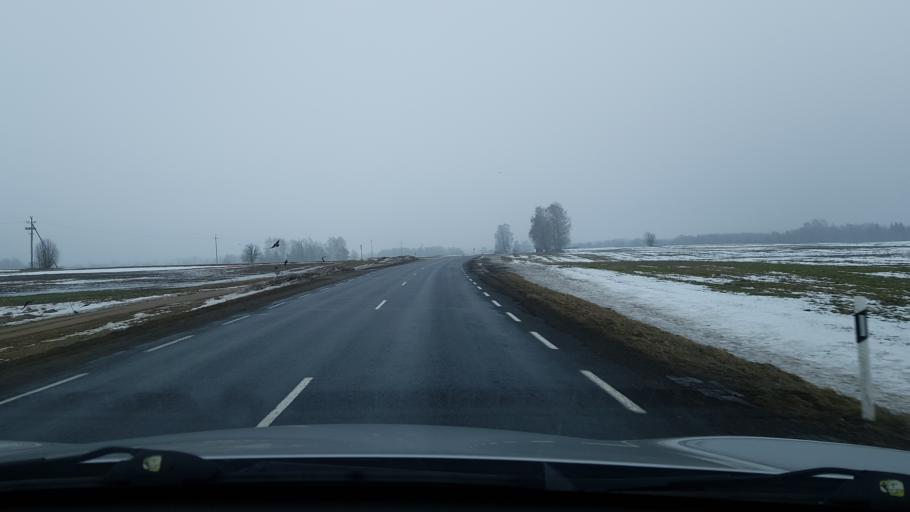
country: EE
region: Viljandimaa
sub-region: Viiratsi vald
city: Viiratsi
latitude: 58.2592
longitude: 25.7135
